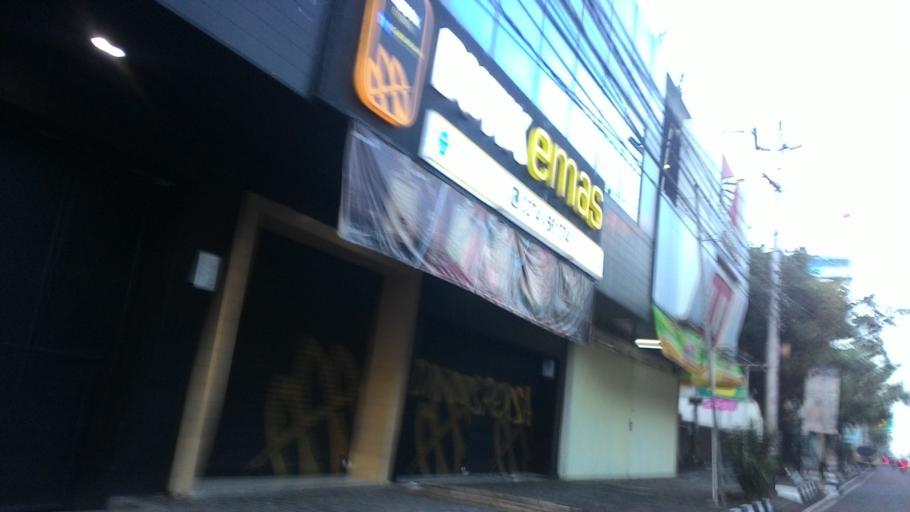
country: ID
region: Daerah Istimewa Yogyakarta
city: Yogyakarta
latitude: -7.7832
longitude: 110.3901
